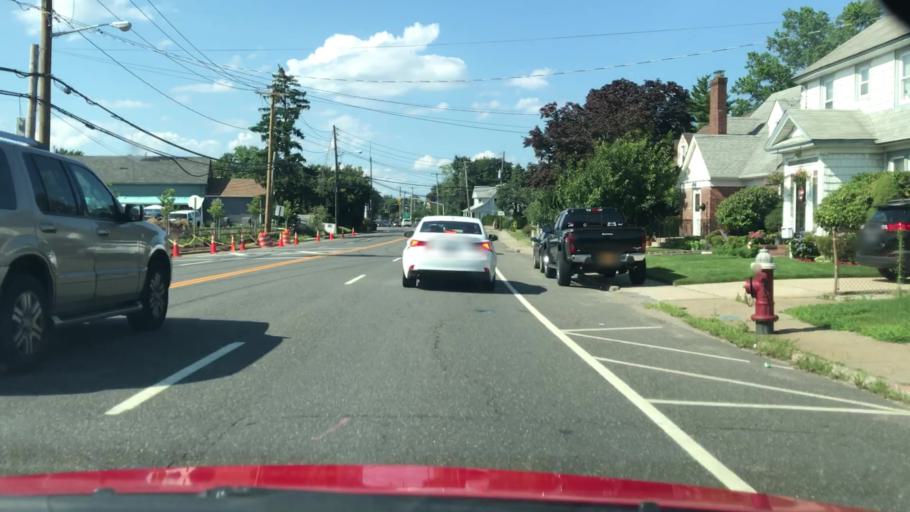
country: US
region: New York
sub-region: Nassau County
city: Malverne
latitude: 40.6785
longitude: -73.6641
